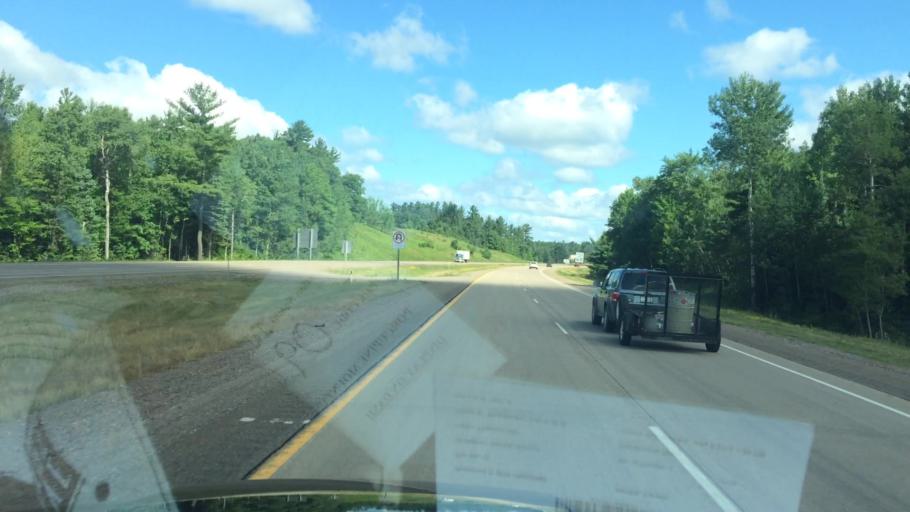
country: US
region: Wisconsin
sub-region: Lincoln County
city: Tomahawk
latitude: 45.4257
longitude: -89.6760
